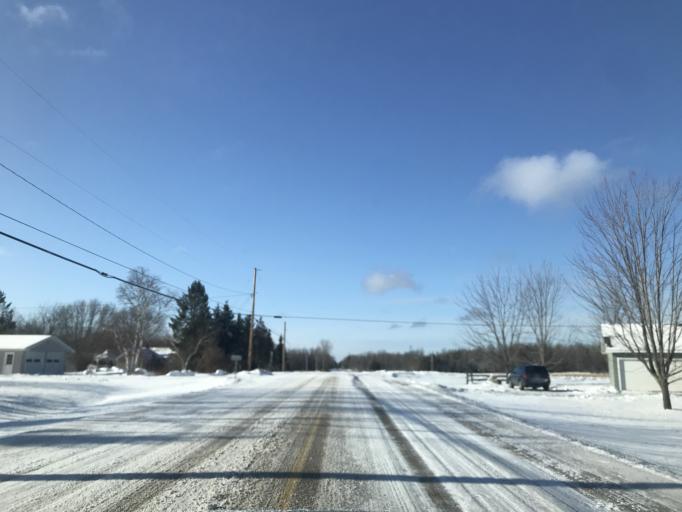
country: US
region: Wisconsin
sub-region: Door County
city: Sturgeon Bay
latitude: 44.8497
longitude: -87.4777
